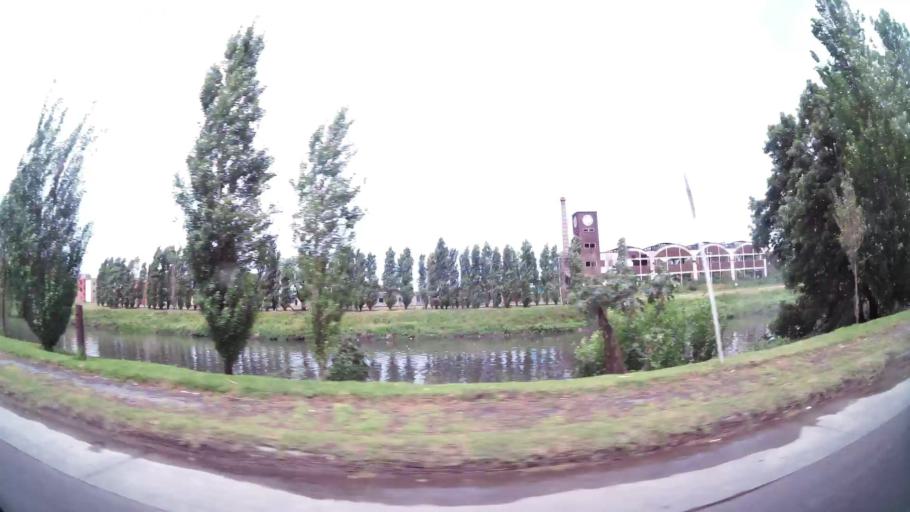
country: AR
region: Buenos Aires F.D.
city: Villa Lugano
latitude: -34.6780
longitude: -58.4386
